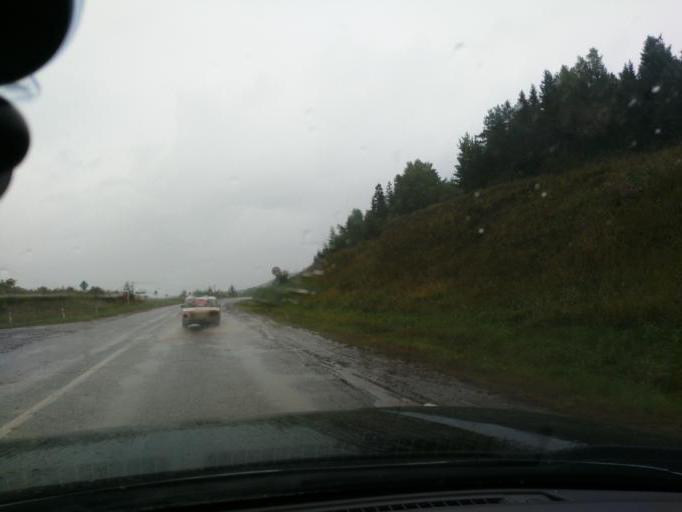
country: RU
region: Perm
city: Osa
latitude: 57.2044
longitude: 55.5890
